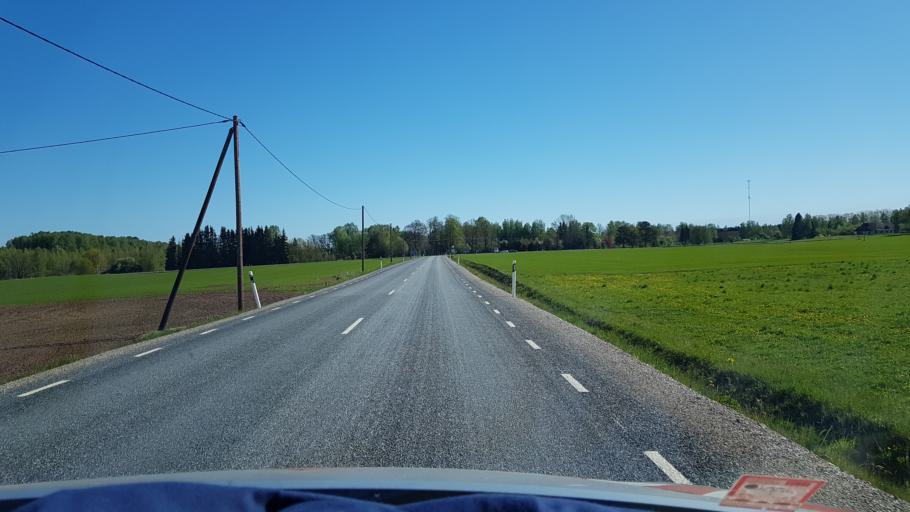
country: EE
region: Polvamaa
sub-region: Polva linn
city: Polva
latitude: 58.1531
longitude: 27.1779
